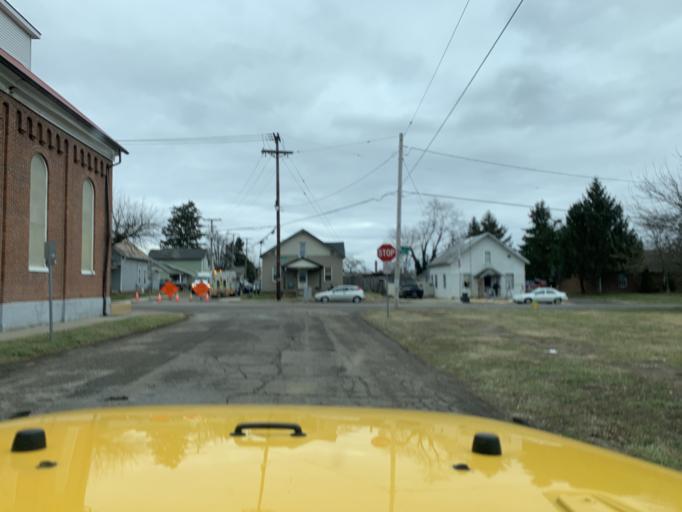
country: US
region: Ohio
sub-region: Licking County
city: Newark
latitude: 40.0529
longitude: -82.4046
